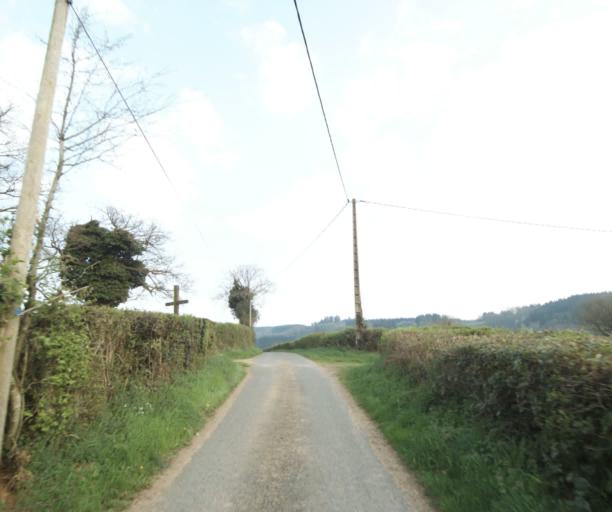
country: FR
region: Bourgogne
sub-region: Departement de Saone-et-Loire
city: Matour
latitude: 46.4258
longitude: 4.4667
